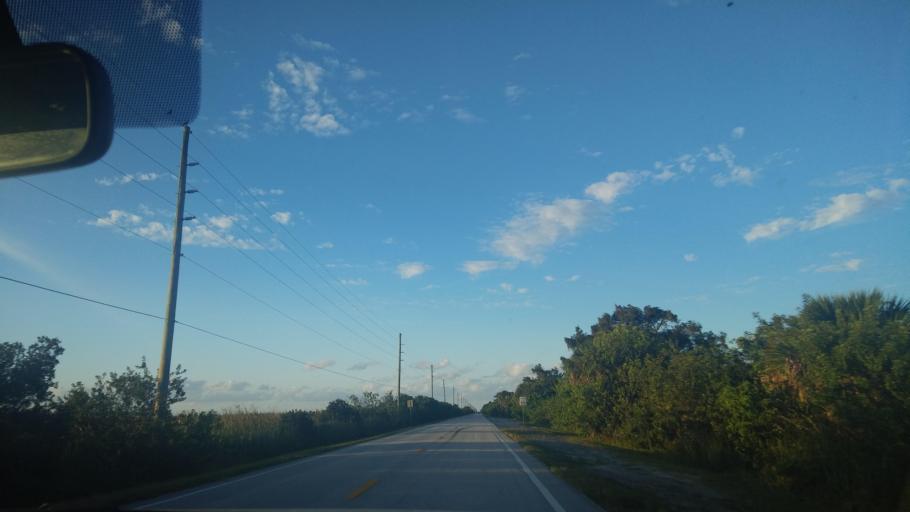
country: US
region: Florida
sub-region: Indian River County
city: Fellsmere
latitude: 27.6706
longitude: -80.6431
